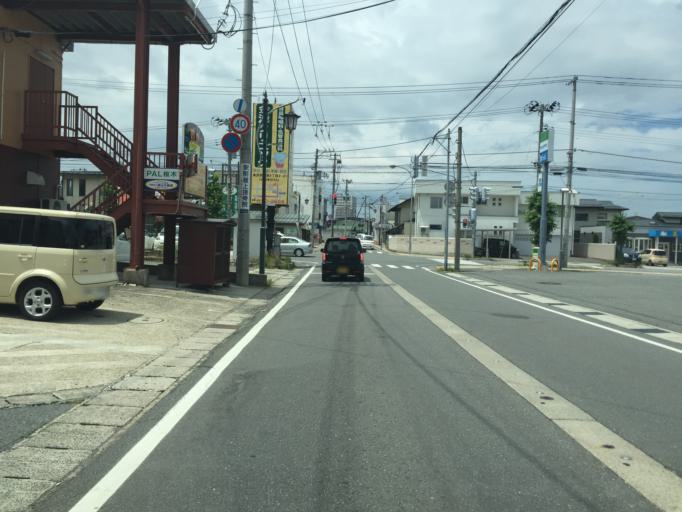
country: JP
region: Yamagata
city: Yonezawa
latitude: 37.9151
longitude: 140.1176
